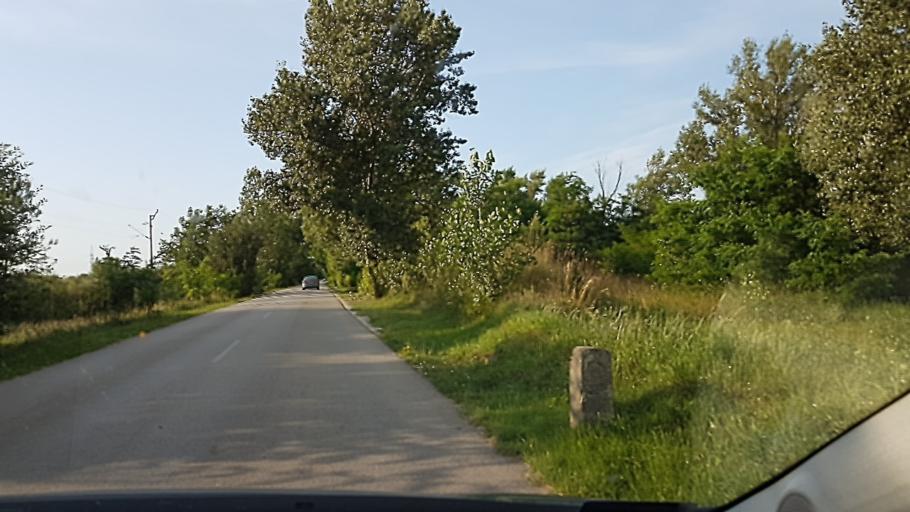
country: HU
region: Pest
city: Dunavarsany
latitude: 47.2629
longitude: 19.0630
